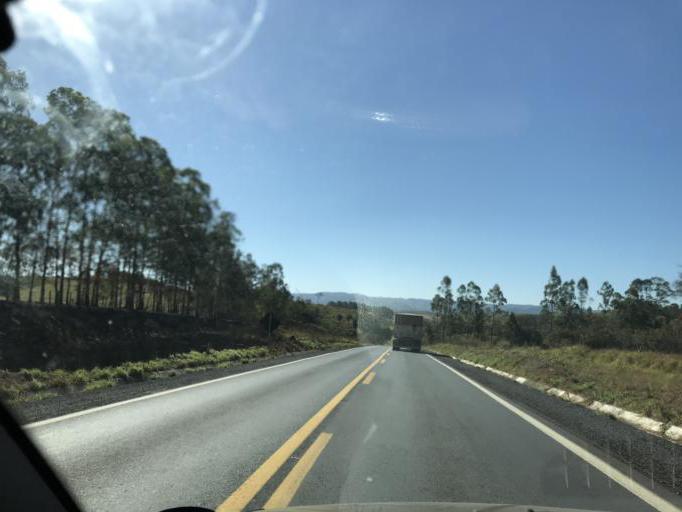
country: BR
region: Minas Gerais
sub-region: Bambui
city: Bambui
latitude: -19.8658
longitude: -45.9854
